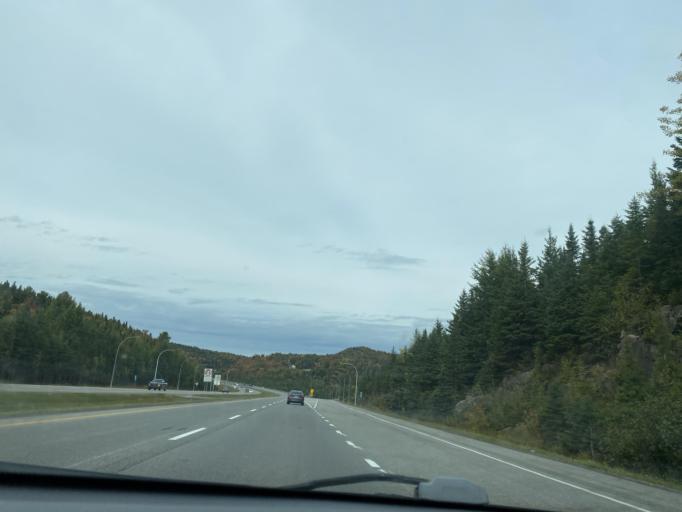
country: CA
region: Quebec
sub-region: Laurentides
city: Val-David
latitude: 46.0062
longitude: -74.2287
